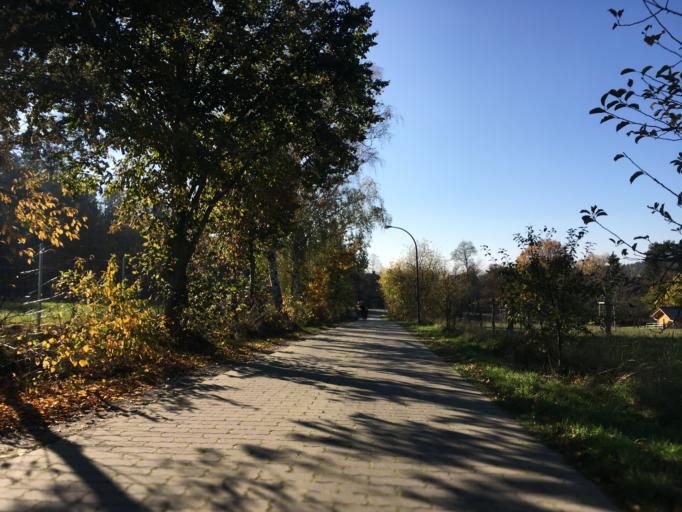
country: DE
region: Brandenburg
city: Reichenwalde
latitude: 52.2885
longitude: 14.0120
